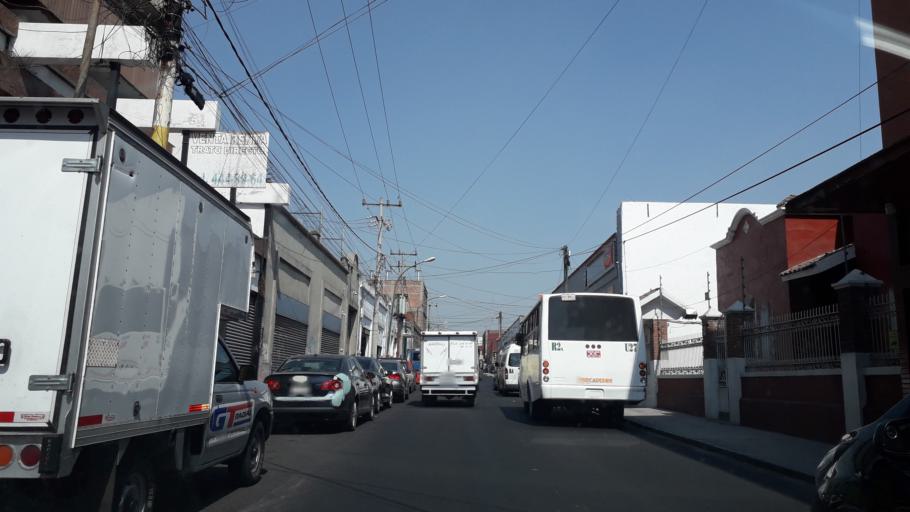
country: MX
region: Puebla
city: Puebla
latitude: 19.0507
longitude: -98.2088
